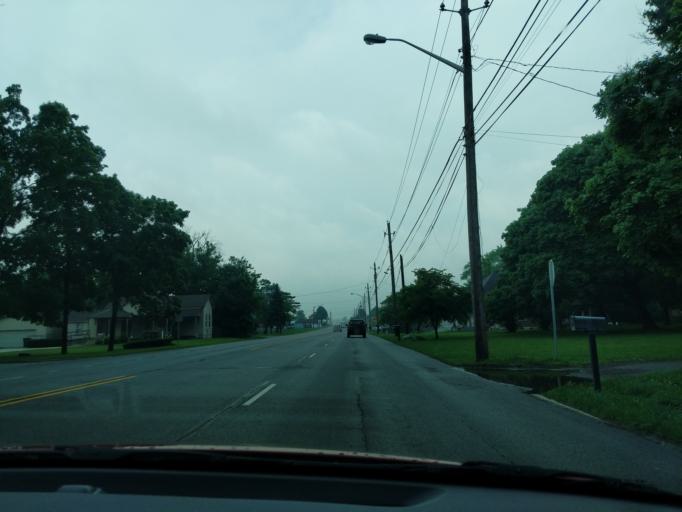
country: US
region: Indiana
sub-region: Hancock County
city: McCordsville
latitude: 39.8949
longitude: -85.9213
